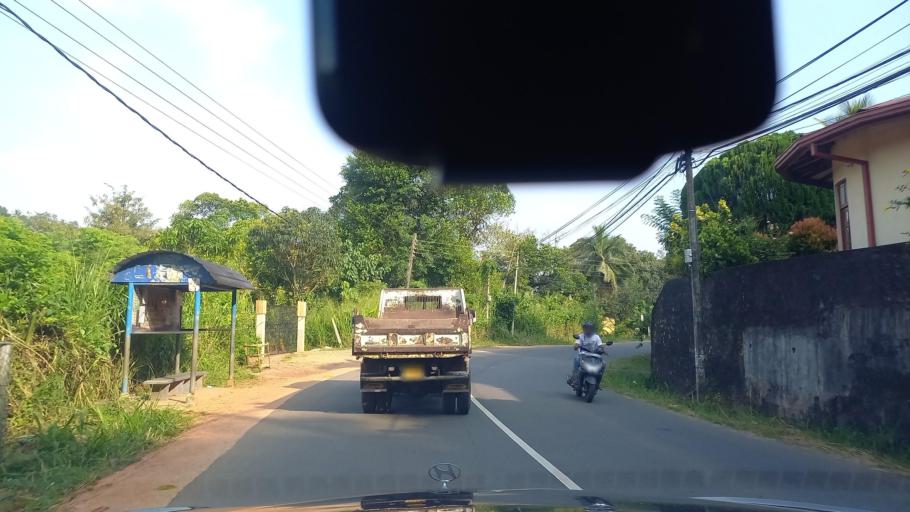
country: LK
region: Central
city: Kandy
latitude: 7.2362
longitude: 80.6020
